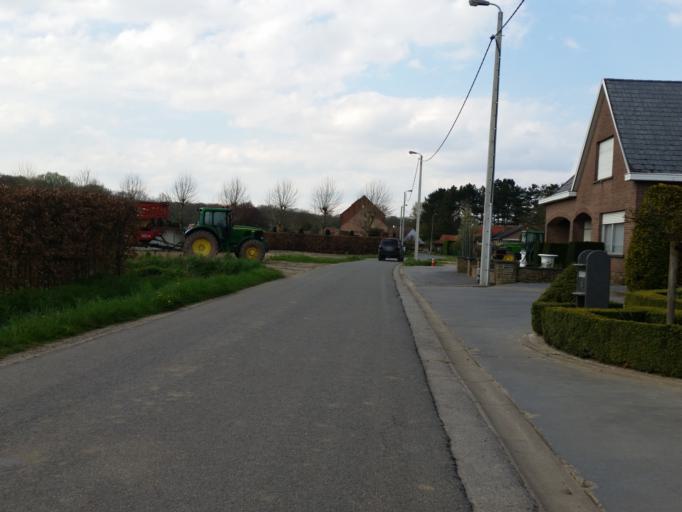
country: BE
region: Flanders
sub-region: Provincie Vlaams-Brabant
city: Kampenhout
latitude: 50.9482
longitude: 4.5211
